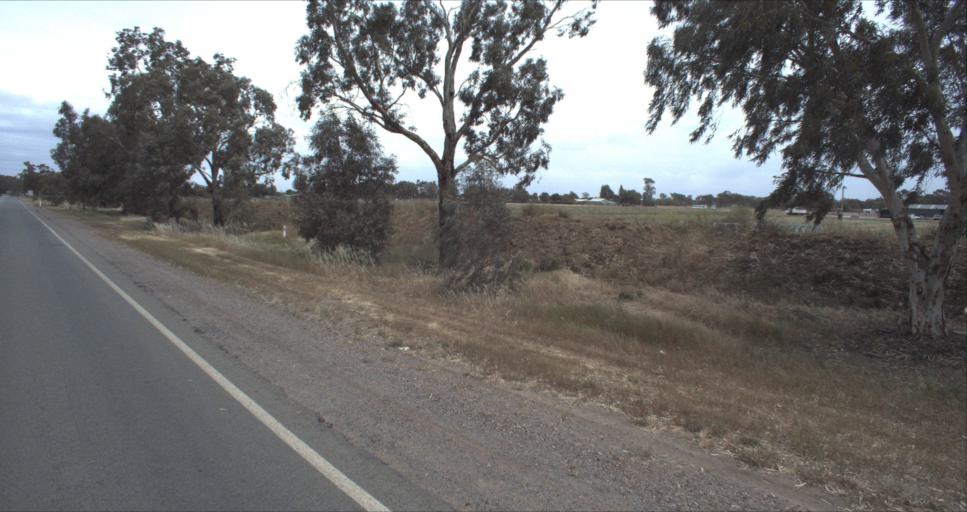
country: AU
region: New South Wales
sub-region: Leeton
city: Leeton
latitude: -34.5304
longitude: 146.4096
